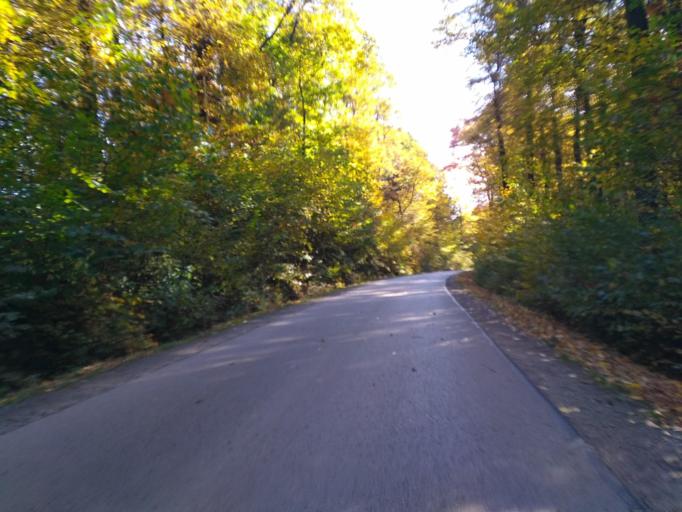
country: PL
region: Subcarpathian Voivodeship
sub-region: Powiat ropczycko-sedziszowski
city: Iwierzyce
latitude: 50.0467
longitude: 21.7729
